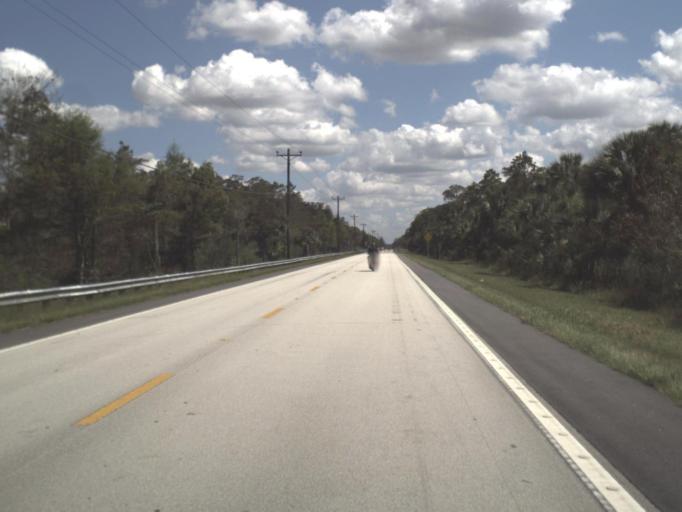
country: US
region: Florida
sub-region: Collier County
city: Marco
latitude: 25.8980
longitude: -81.2863
